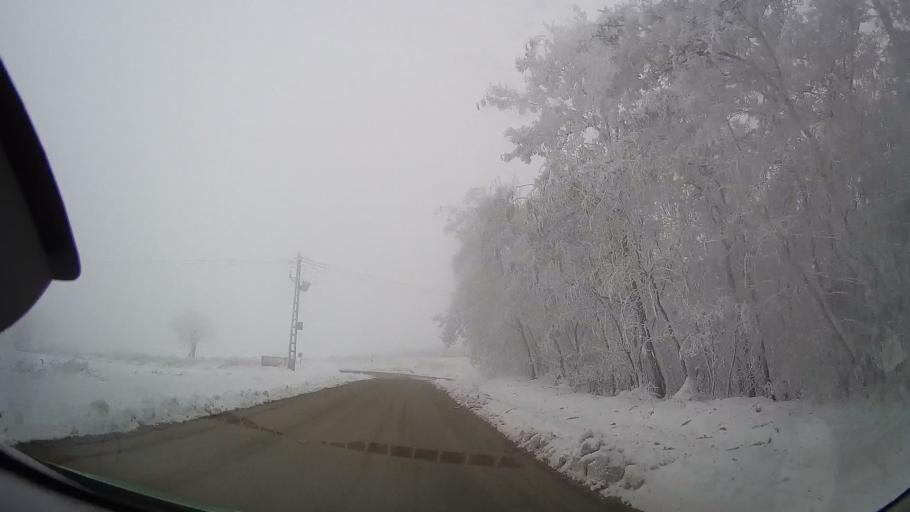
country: RO
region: Iasi
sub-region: Comuna Tansa
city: Suhulet
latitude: 46.8961
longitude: 27.2443
